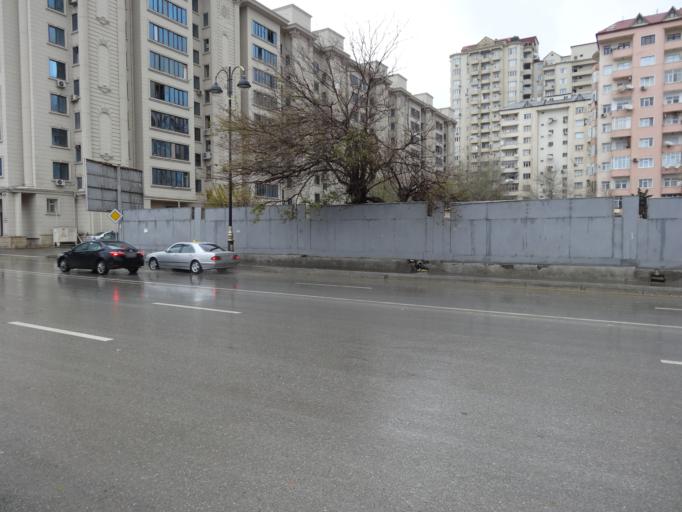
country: AZ
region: Baki
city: Baku
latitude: 40.3989
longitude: 49.8669
